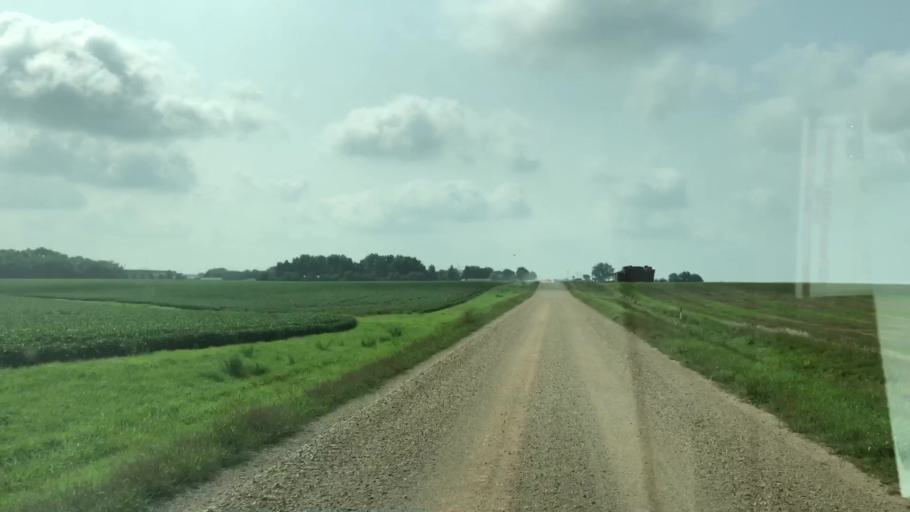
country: US
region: Iowa
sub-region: O'Brien County
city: Sheldon
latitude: 43.1916
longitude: -95.8821
